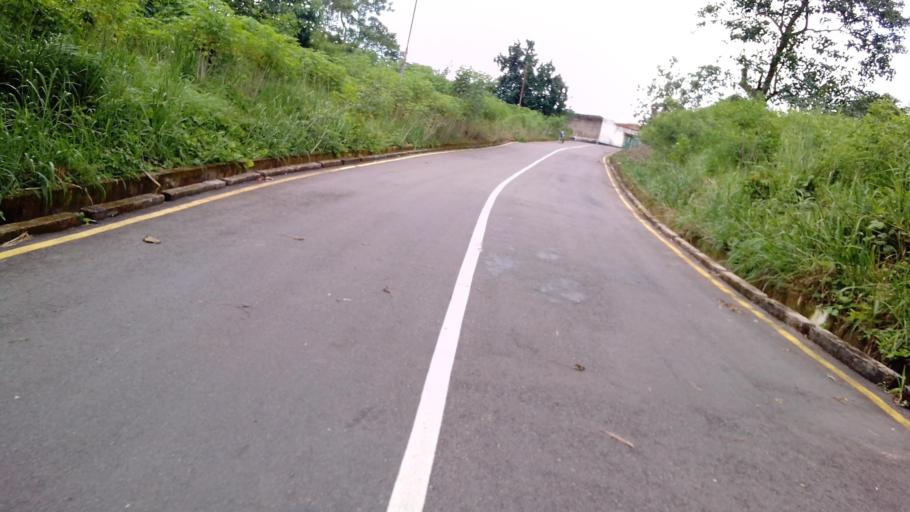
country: SL
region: Eastern Province
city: Koidu
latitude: 8.6537
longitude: -10.9847
